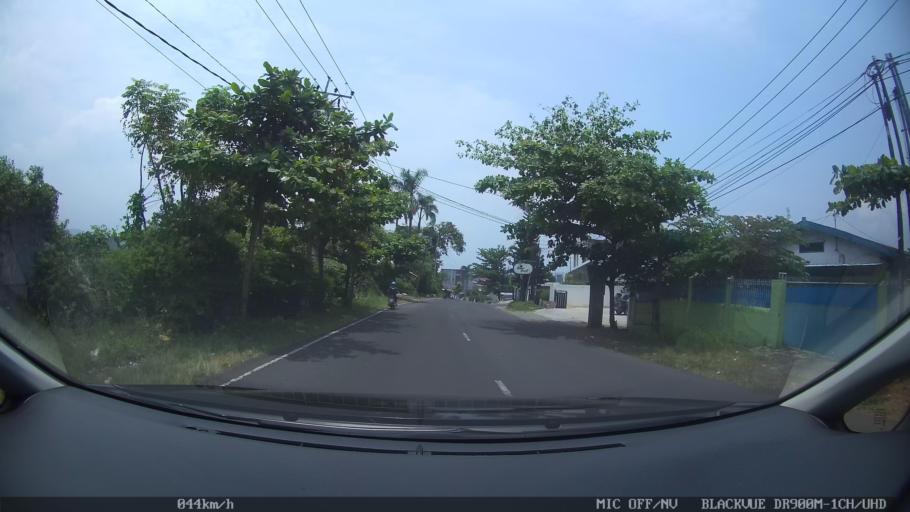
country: ID
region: Lampung
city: Bandarlampung
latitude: -5.4350
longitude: 105.2739
